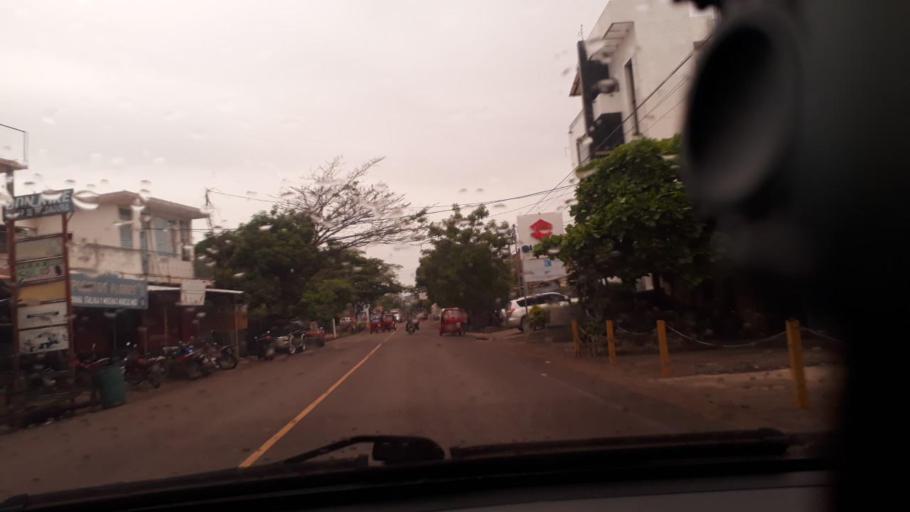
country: GT
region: Jutiapa
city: Asuncion Mita
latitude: 14.3318
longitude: -89.7122
